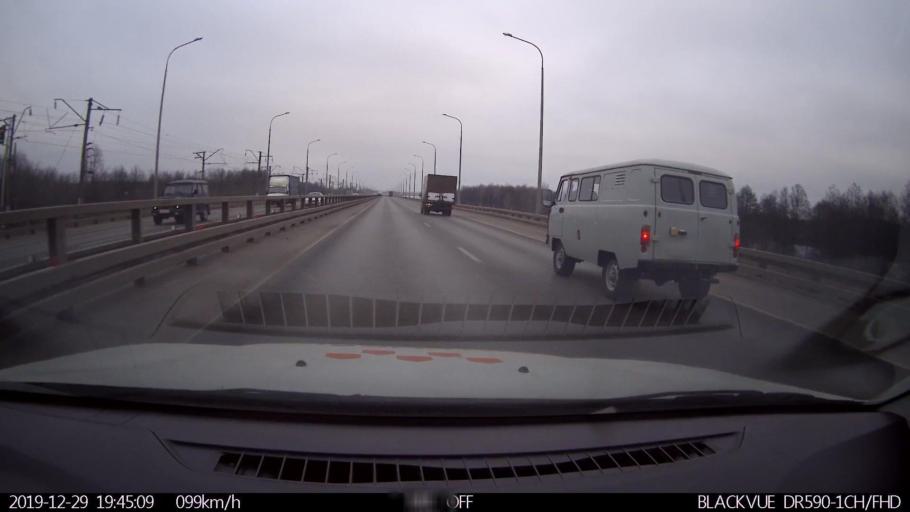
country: RU
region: Nizjnij Novgorod
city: Neklyudovo
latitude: 56.3850
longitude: 43.9656
